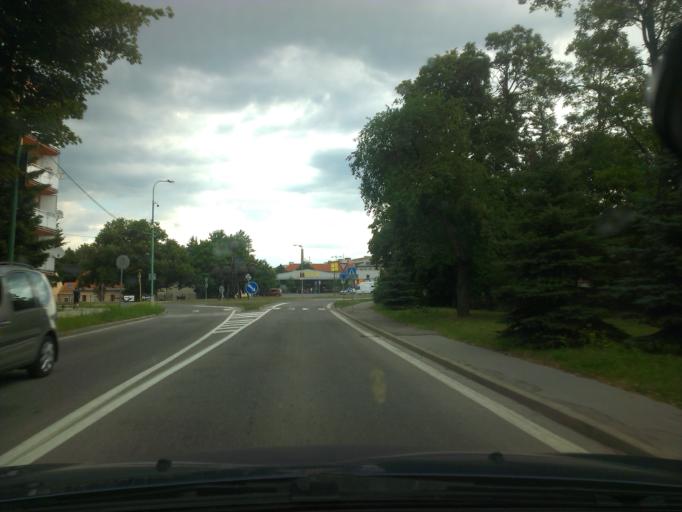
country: SK
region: Trenciansky
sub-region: Okres Myjava
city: Myjava
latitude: 48.7548
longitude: 17.5675
